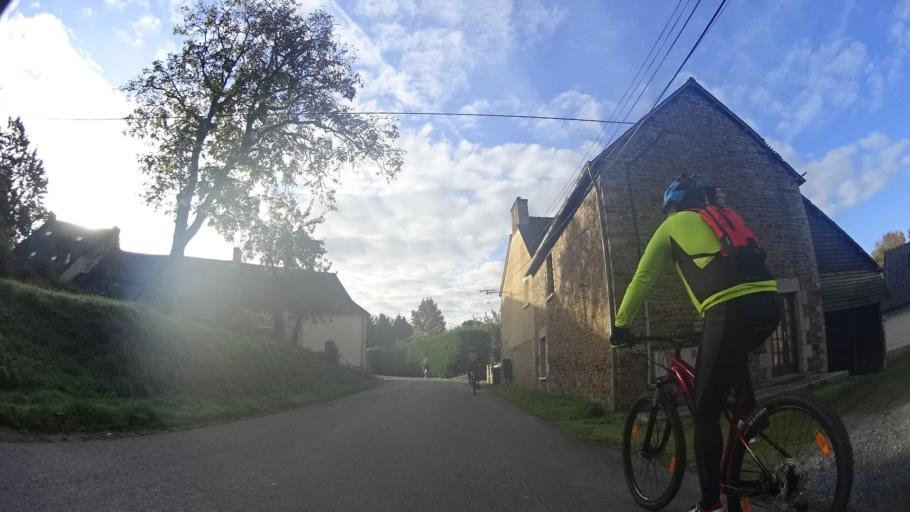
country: FR
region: Brittany
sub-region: Departement des Cotes-d'Armor
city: Evran
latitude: 48.3610
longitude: -1.9510
